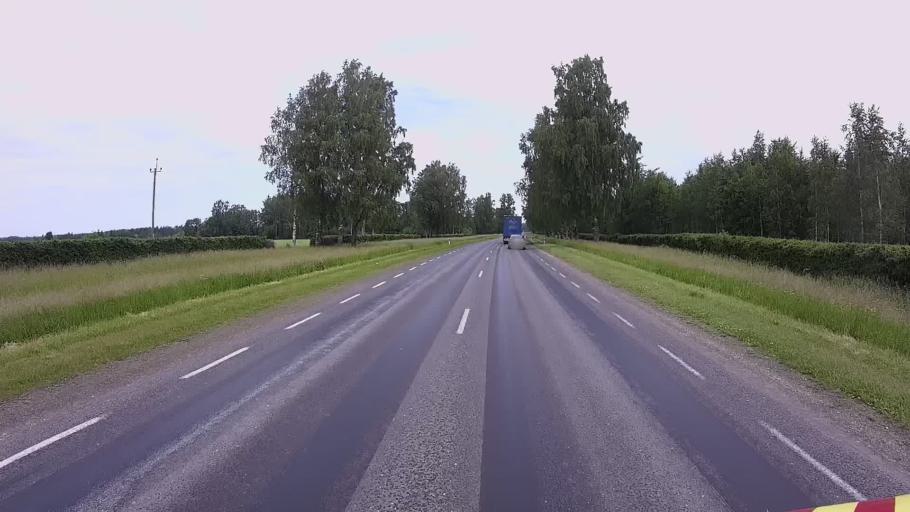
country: EE
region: Viljandimaa
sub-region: Viljandi linn
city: Viljandi
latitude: 58.3122
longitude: 25.5727
